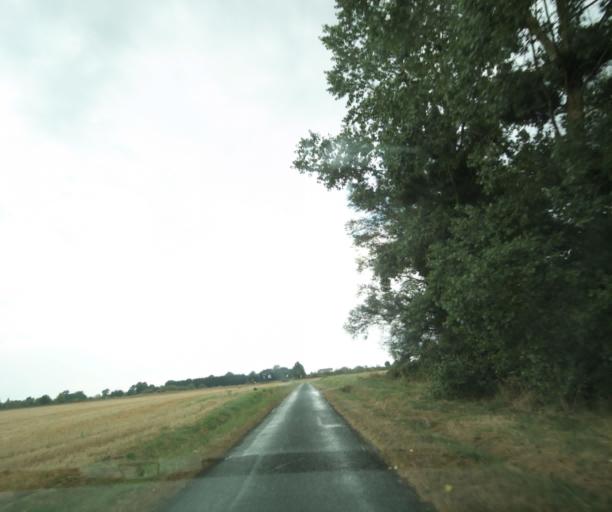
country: FR
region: Poitou-Charentes
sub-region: Departement de la Charente-Maritime
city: Tonnay-Charente
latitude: 45.9465
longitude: -0.8700
